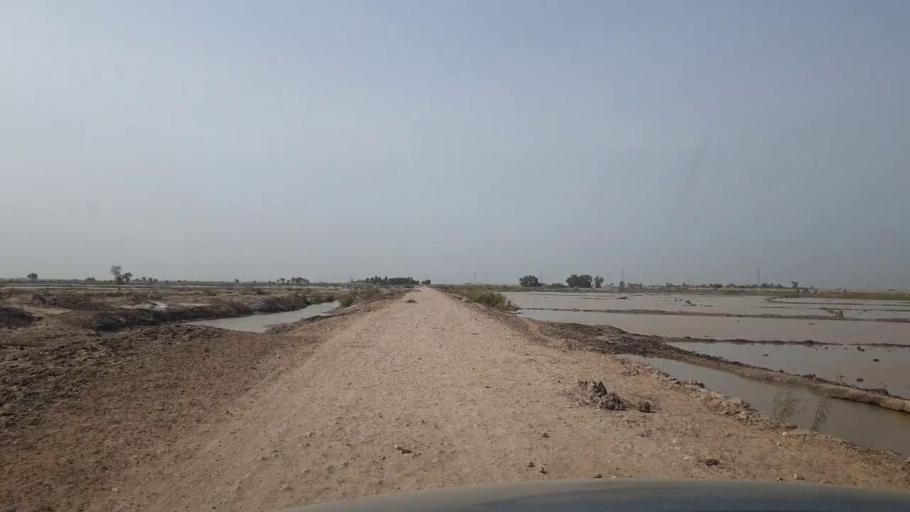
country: PK
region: Sindh
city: Lakhi
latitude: 27.8411
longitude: 68.6997
